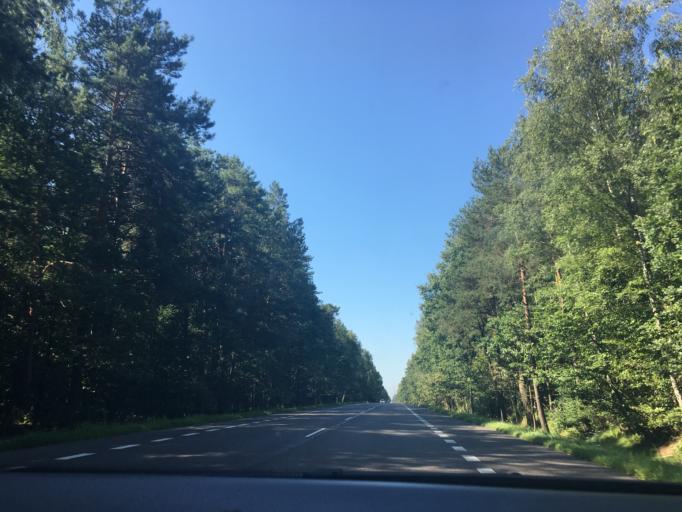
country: PL
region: Lublin Voivodeship
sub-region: Powiat radzynski
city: Borki
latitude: 51.7452
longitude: 22.5563
